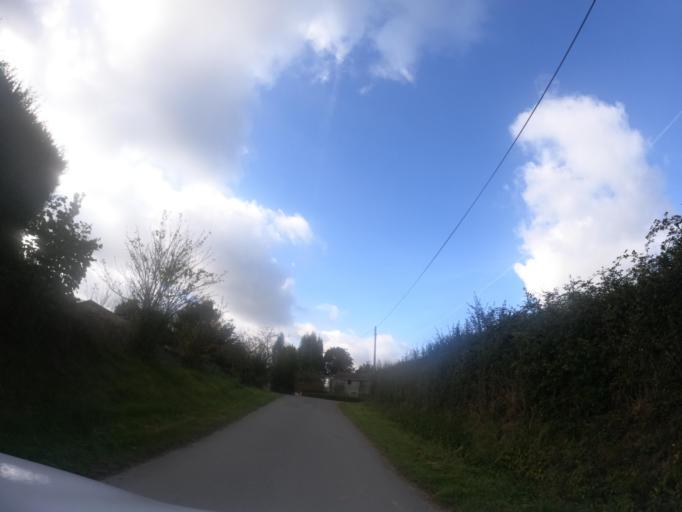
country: FR
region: Poitou-Charentes
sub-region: Departement des Deux-Sevres
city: Courlay
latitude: 46.7810
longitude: -0.6038
